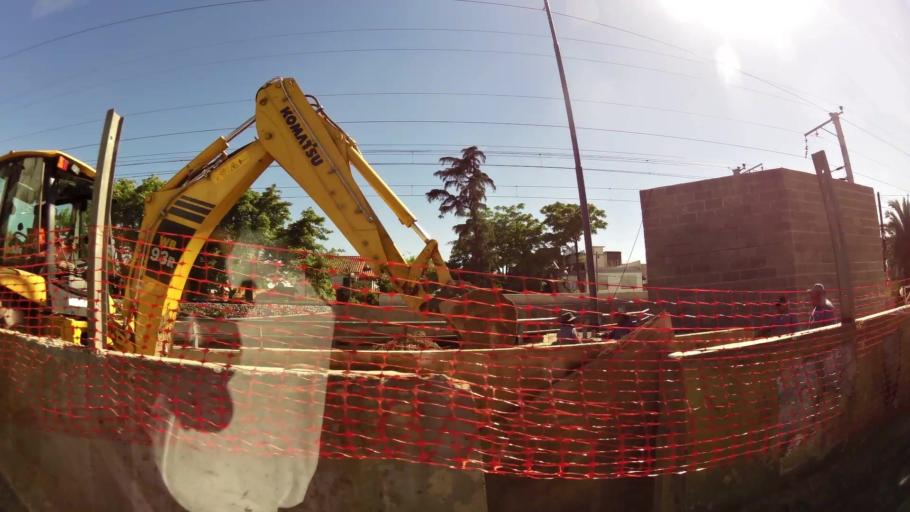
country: AR
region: Buenos Aires
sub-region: Partido de Quilmes
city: Quilmes
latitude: -34.7028
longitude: -58.2988
